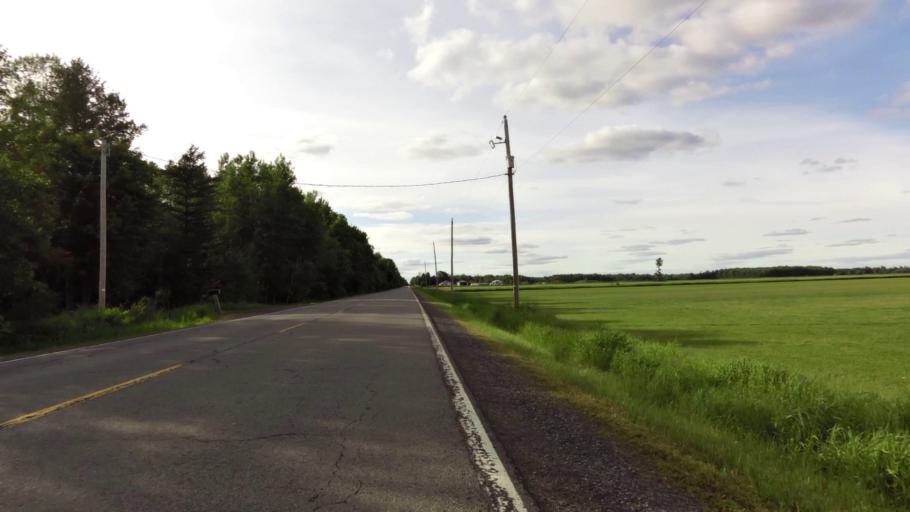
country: CA
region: Ontario
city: Ottawa
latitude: 45.1919
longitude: -75.5866
